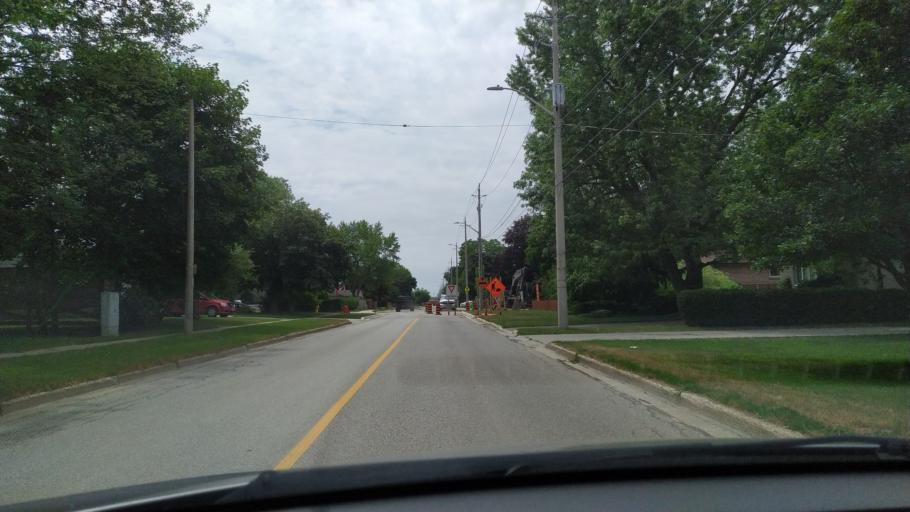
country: CA
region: Ontario
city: Stratford
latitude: 43.3646
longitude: -80.9964
